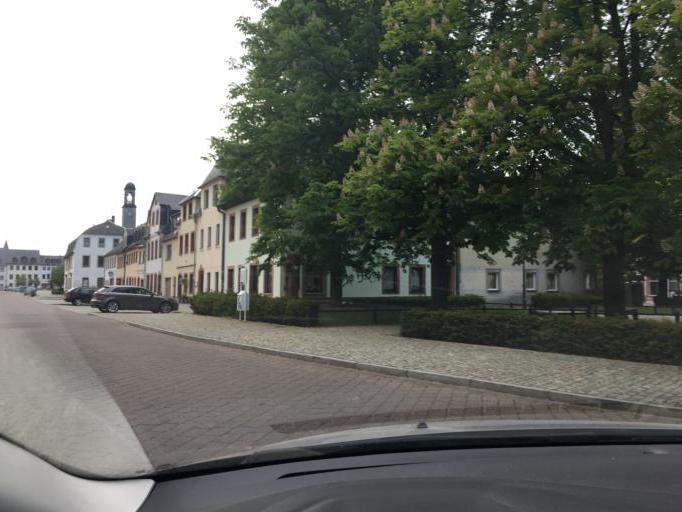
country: DE
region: Saxony
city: Rochlitz
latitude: 51.0456
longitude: 12.8021
